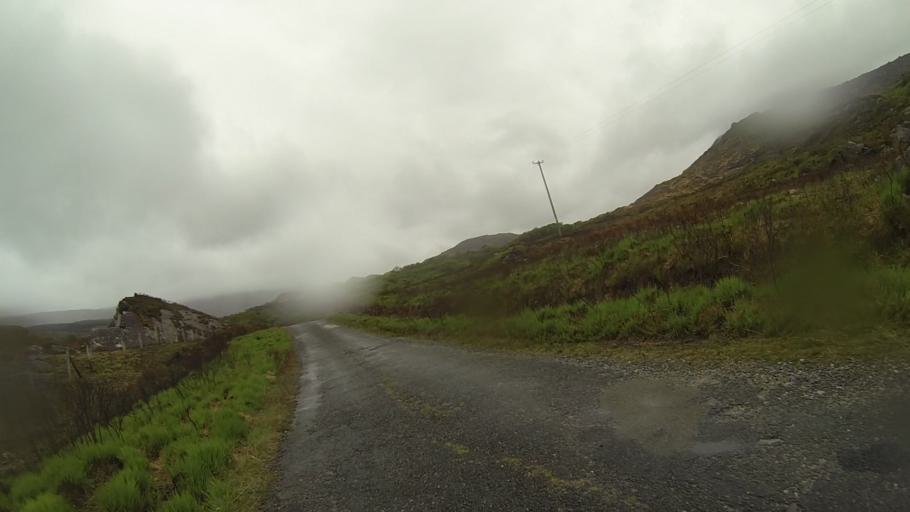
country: IE
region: Munster
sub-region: Ciarrai
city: Kenmare
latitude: 51.9687
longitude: -9.6366
